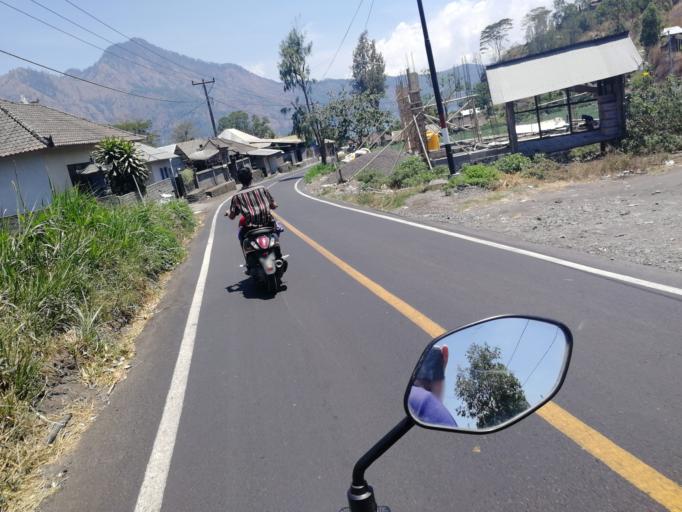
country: ID
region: Bali
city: Banjar Trunyan
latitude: -8.2361
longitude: 115.4059
